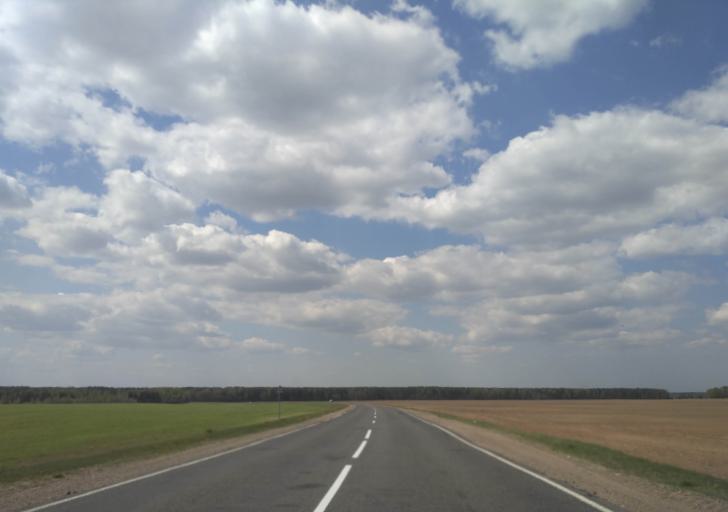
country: BY
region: Minsk
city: Vilyeyka
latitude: 54.5175
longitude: 27.0294
